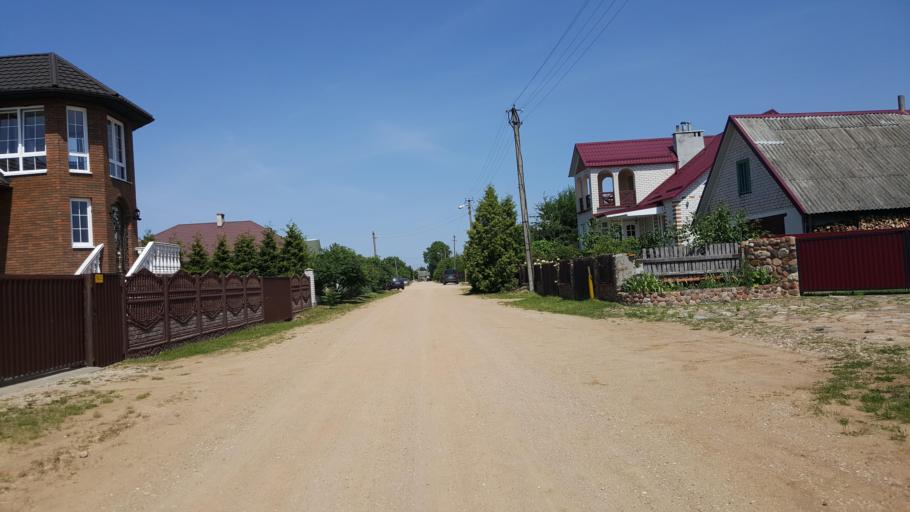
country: BY
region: Brest
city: Vysokaye
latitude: 52.3600
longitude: 23.3895
